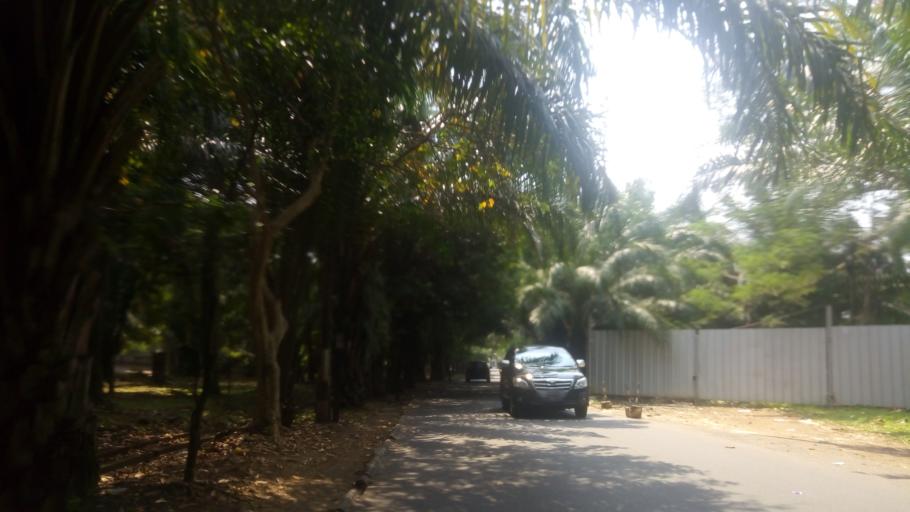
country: ID
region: Jakarta Raya
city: Jakarta
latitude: -6.2372
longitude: 106.8360
